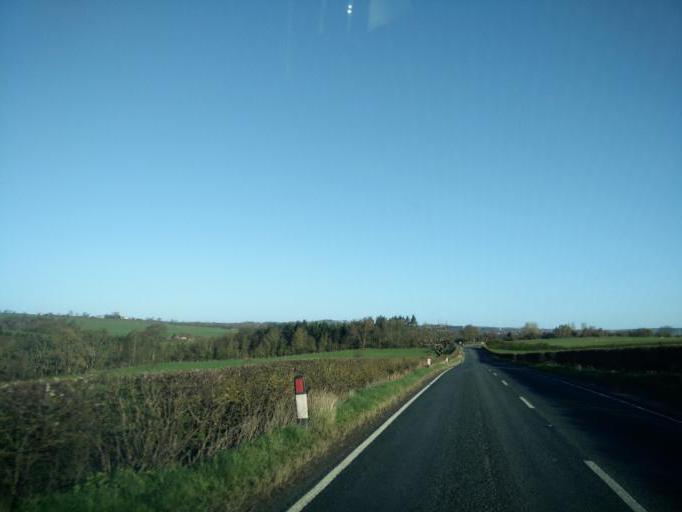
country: GB
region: England
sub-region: County Durham
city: Crook
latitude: 54.6851
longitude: -1.7372
